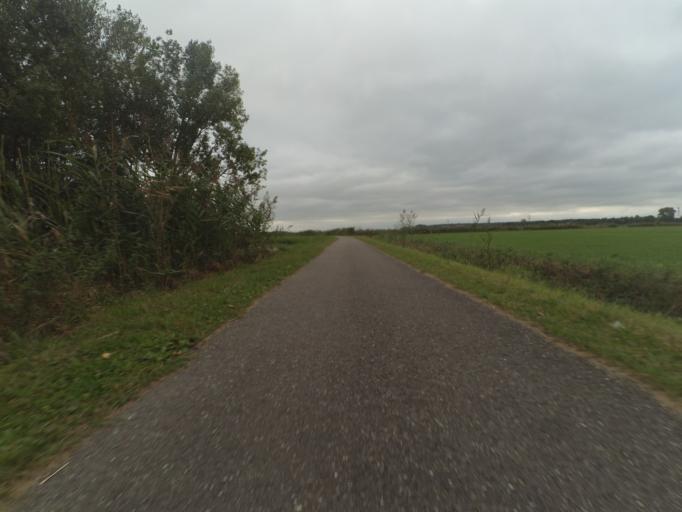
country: NL
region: Utrecht
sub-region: Gemeente Rhenen
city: Rhenen
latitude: 51.9864
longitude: 5.6141
